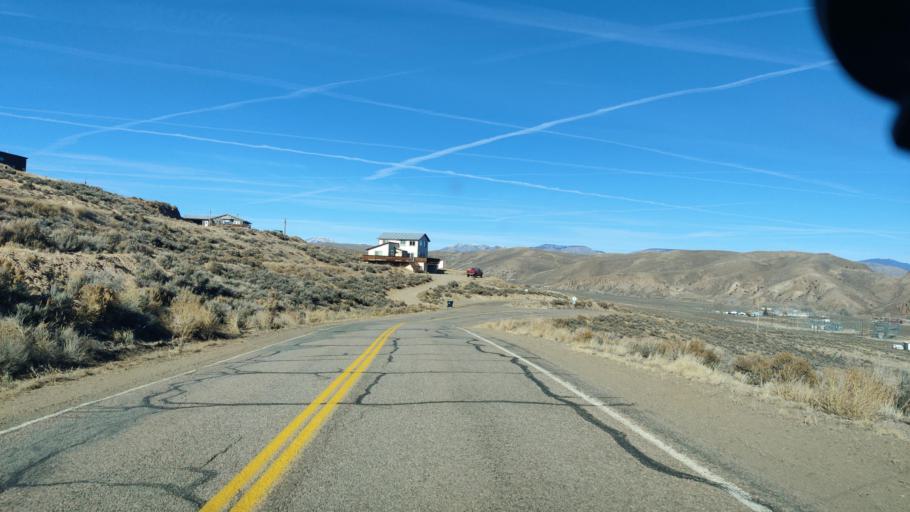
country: US
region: Colorado
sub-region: Gunnison County
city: Gunnison
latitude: 38.5421
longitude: -106.9573
